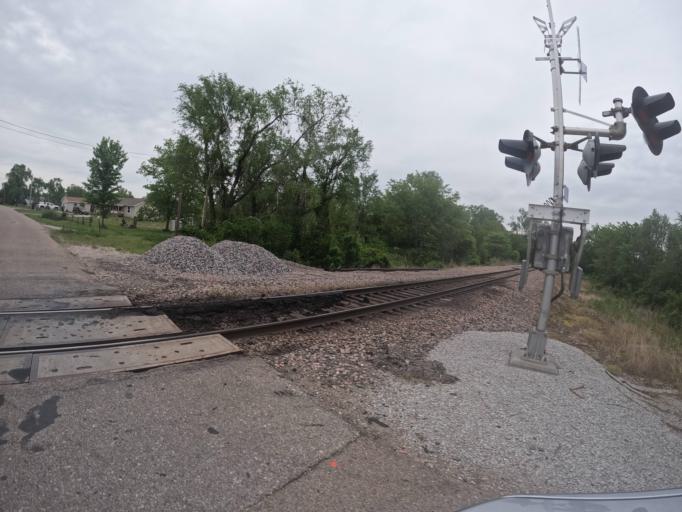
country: US
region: Nebraska
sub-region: Sarpy County
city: Offutt Air Force Base
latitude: 41.0516
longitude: -95.9518
